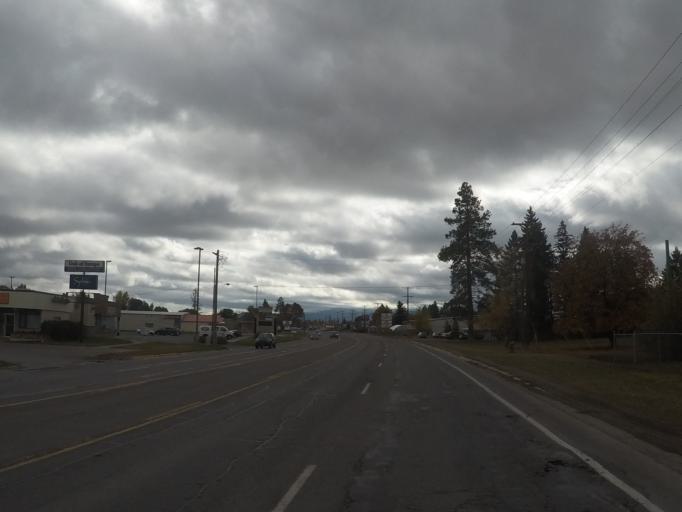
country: US
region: Montana
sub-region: Flathead County
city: Evergreen
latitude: 48.2242
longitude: -114.2770
